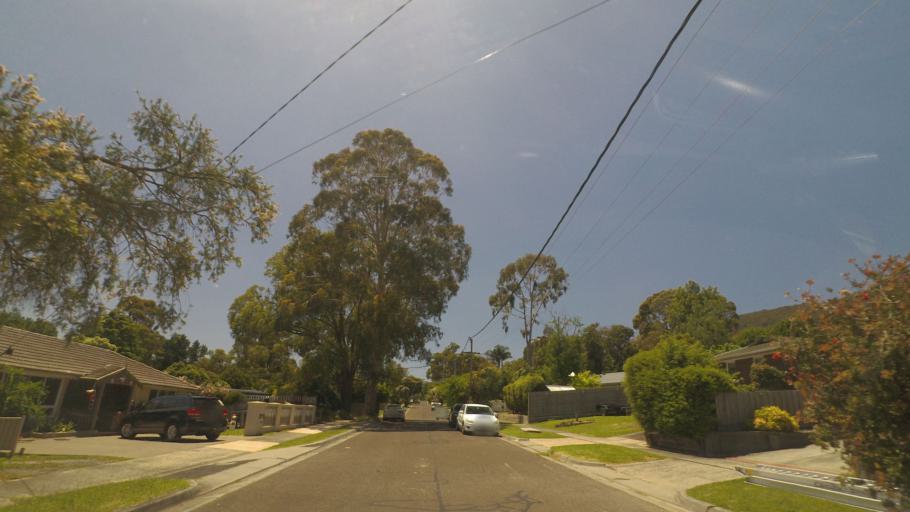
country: AU
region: Victoria
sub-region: Yarra Ranges
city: Montrose
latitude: -37.8155
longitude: 145.3450
